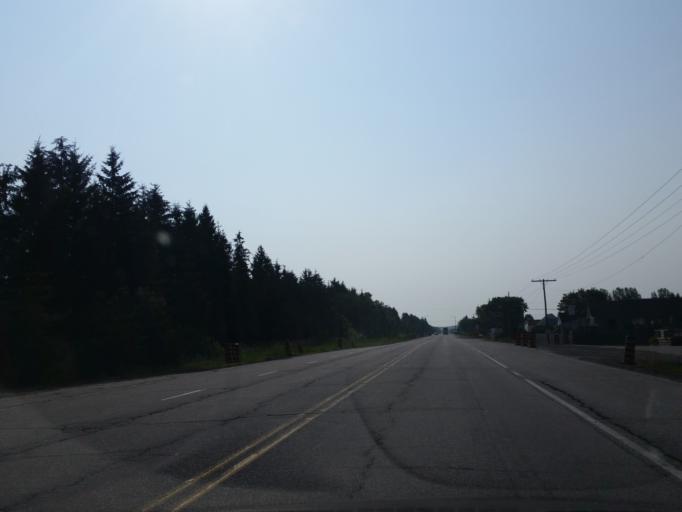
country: CA
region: Ontario
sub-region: Nipissing District
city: North Bay
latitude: 46.4135
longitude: -80.1287
